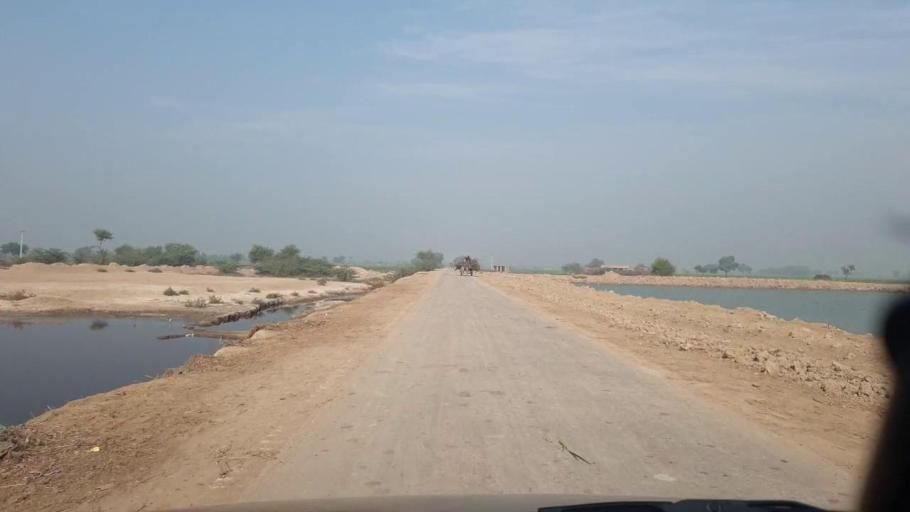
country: PK
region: Sindh
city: Shahdadpur
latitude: 25.9923
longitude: 68.5634
